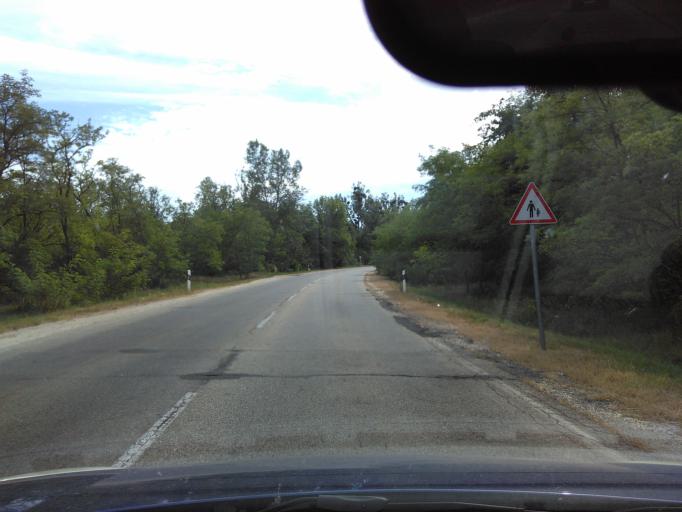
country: HU
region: Pest
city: Godollo
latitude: 47.6021
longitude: 19.4042
